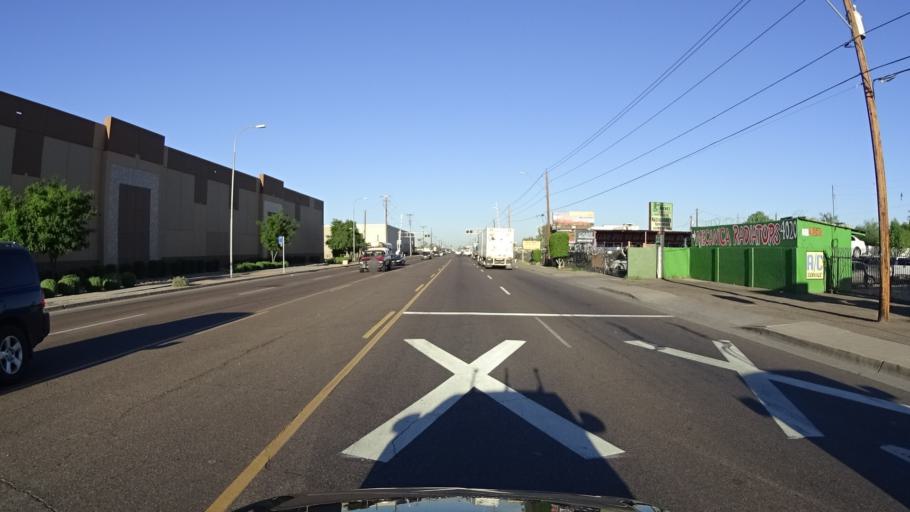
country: US
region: Arizona
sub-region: Maricopa County
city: Phoenix
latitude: 33.4369
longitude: -112.1460
